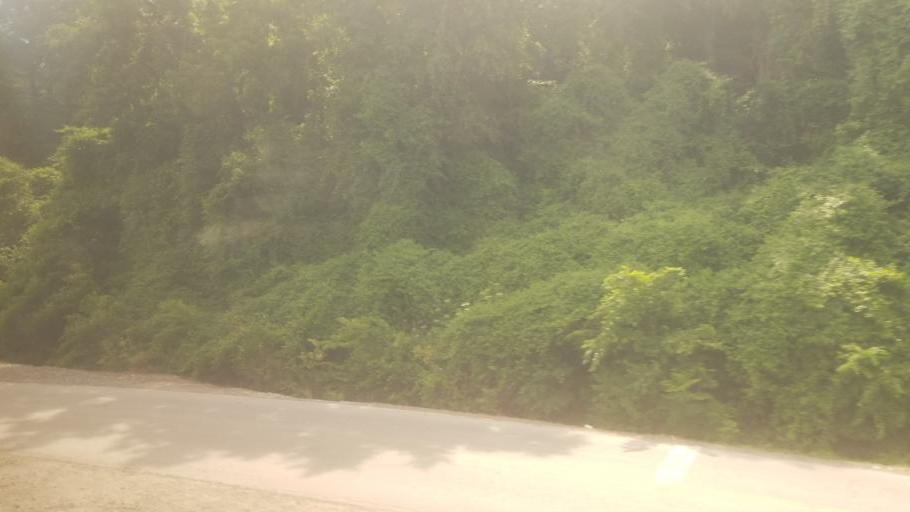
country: US
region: Missouri
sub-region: Jackson County
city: Sugar Creek
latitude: 39.1272
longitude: -94.4380
